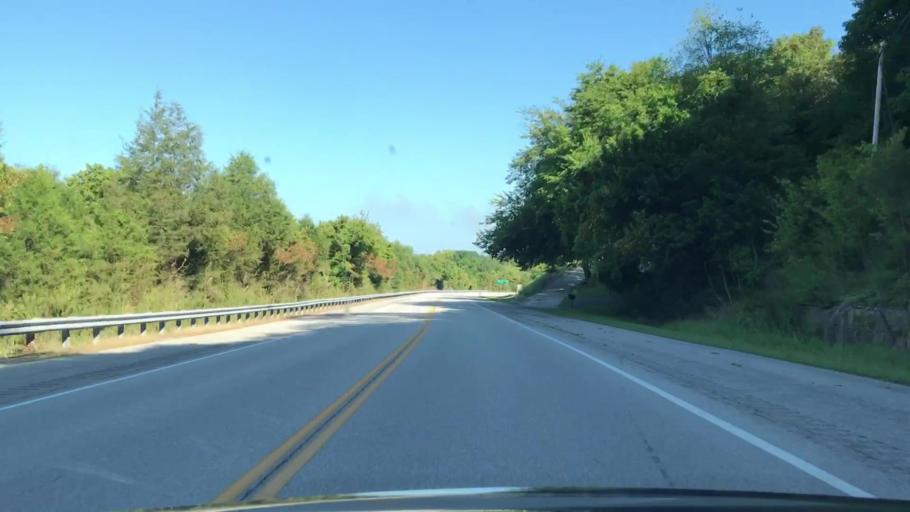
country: US
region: Tennessee
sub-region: Clay County
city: Celina
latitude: 36.4671
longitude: -85.5801
